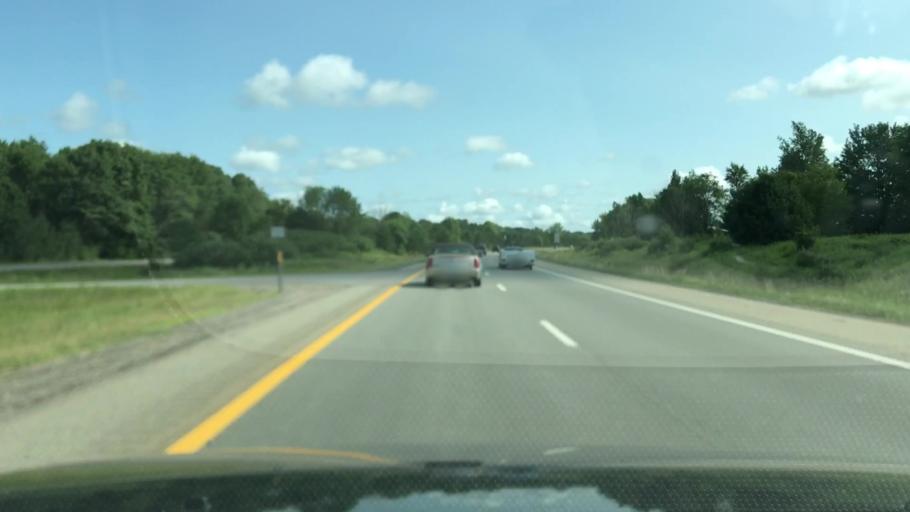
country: US
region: Michigan
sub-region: Kent County
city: Cedar Springs
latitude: 43.3036
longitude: -85.5398
